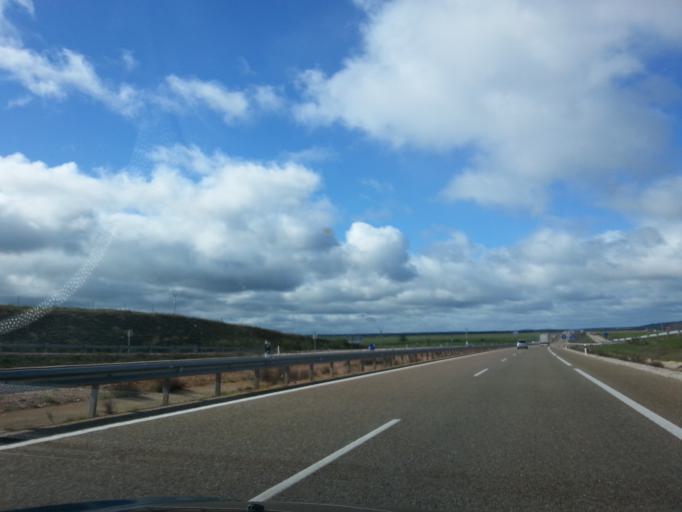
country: ES
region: Castille and Leon
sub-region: Provincia de Salamanca
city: Robliza de Cojos
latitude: 40.8750
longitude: -5.9823
